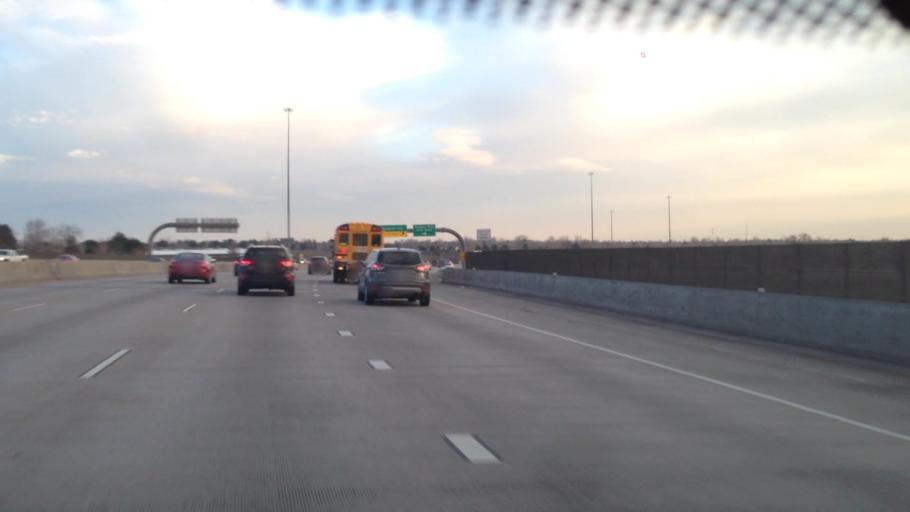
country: US
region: Colorado
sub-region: Adams County
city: Aurora
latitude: 39.6569
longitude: -104.8380
